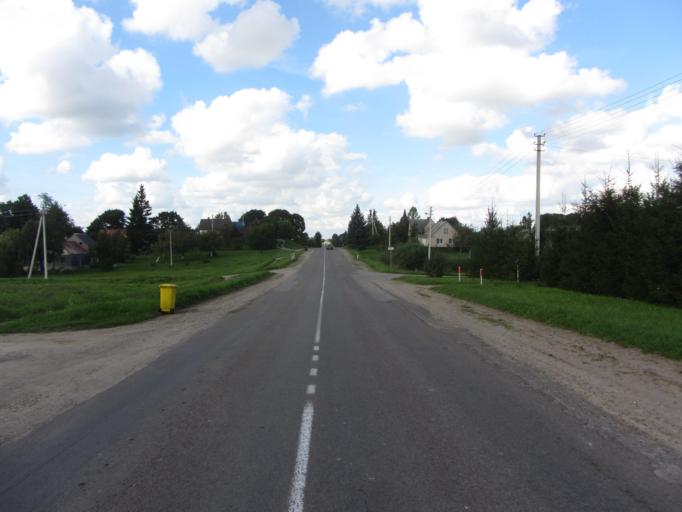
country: LT
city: Vilkija
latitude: 55.0669
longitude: 23.5515
